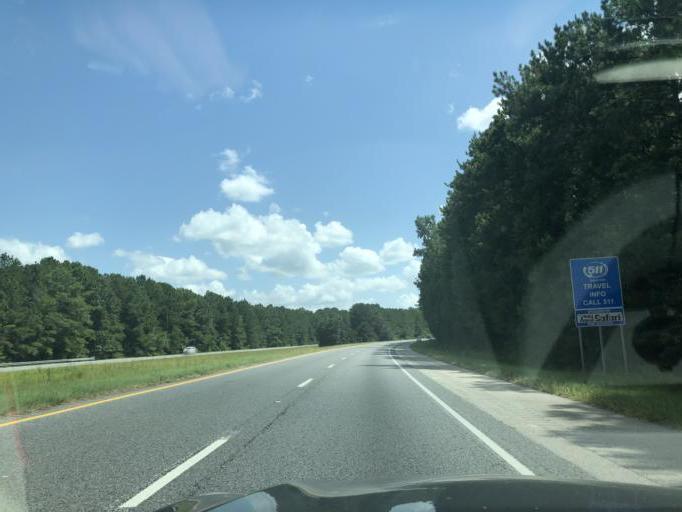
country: US
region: Georgia
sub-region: Troup County
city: La Grange
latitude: 32.9921
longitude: -84.9505
